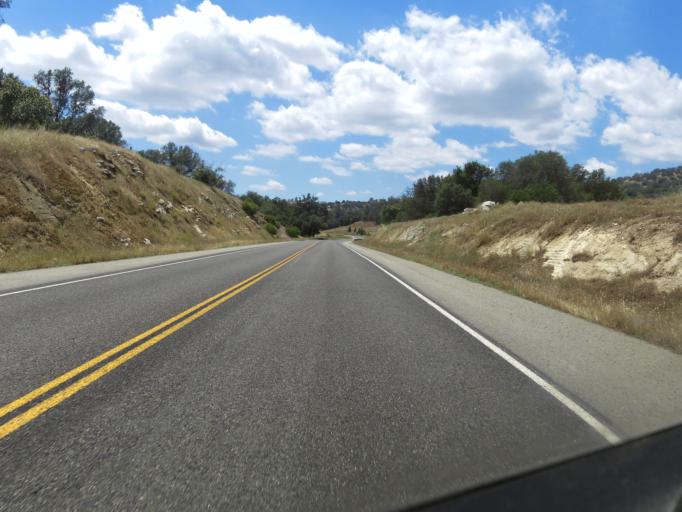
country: US
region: California
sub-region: Madera County
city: Coarsegold
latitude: 37.1521
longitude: -119.6613
